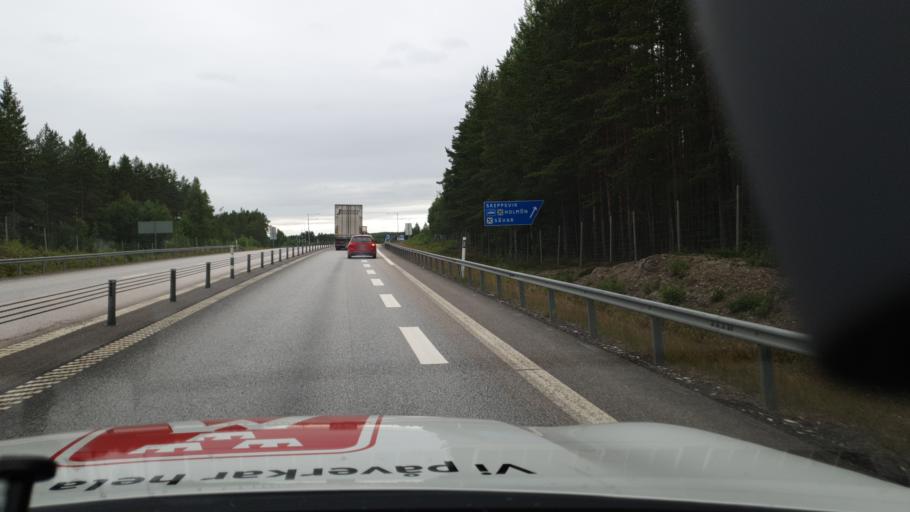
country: SE
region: Vaesterbotten
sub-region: Umea Kommun
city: Saevar
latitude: 63.9018
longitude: 20.5726
